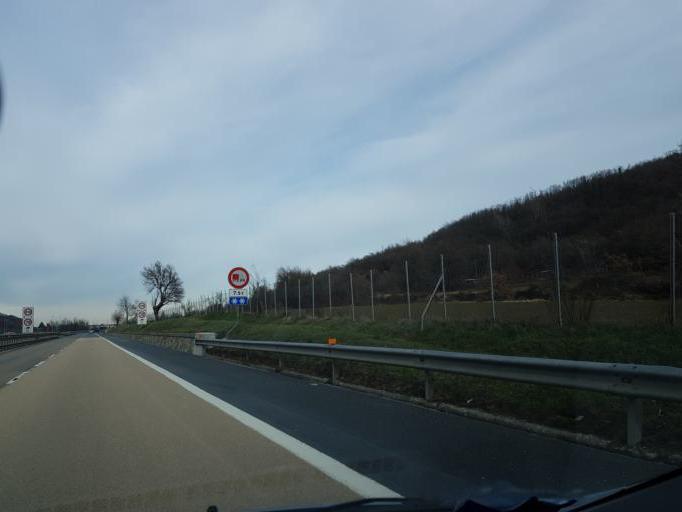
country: IT
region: Piedmont
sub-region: Provincia di Alessandria
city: Arquata Scrivia
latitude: 44.6660
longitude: 8.9099
